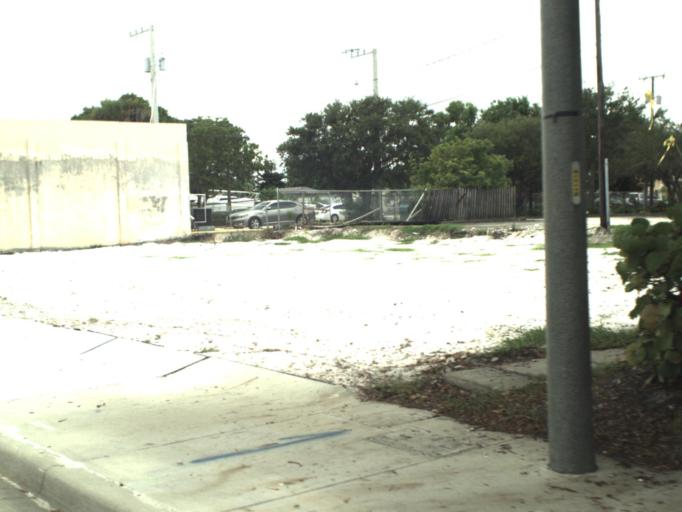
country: US
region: Florida
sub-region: Palm Beach County
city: Riviera Beach
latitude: 26.7768
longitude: -80.0551
